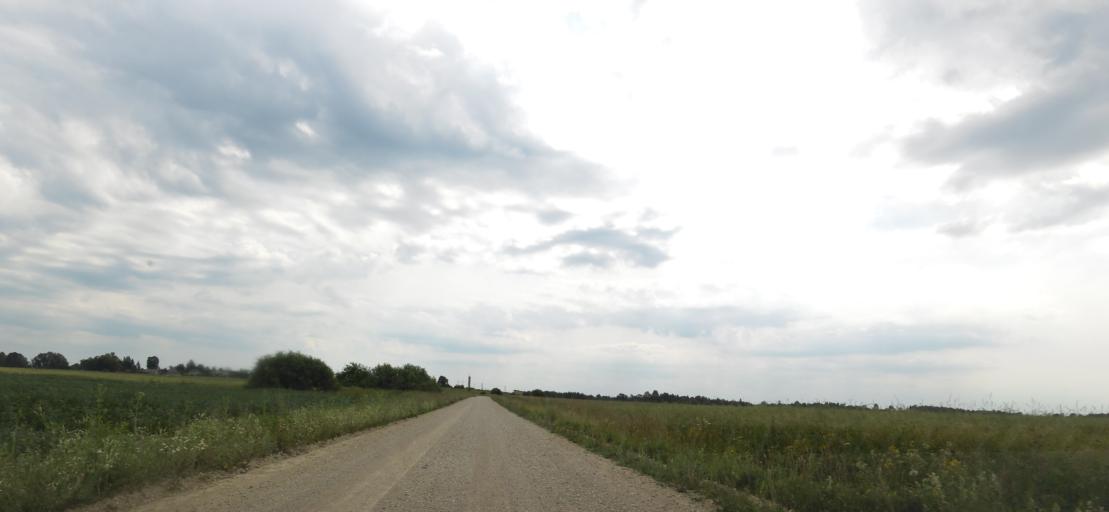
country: LT
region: Panevezys
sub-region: Birzai
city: Birzai
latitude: 56.4201
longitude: 24.8821
